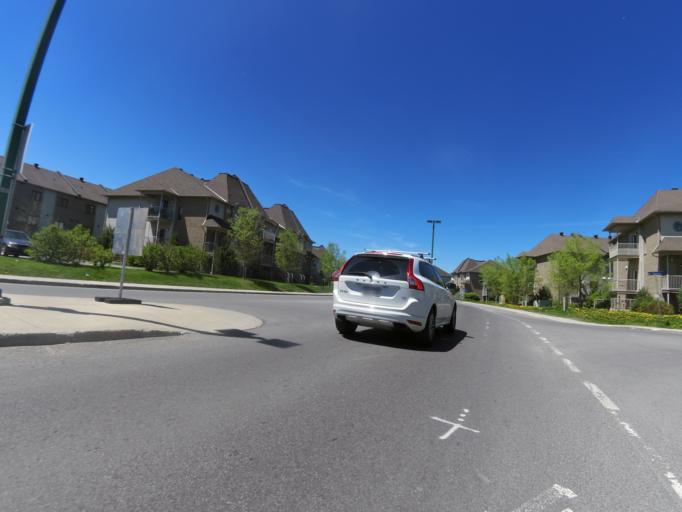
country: CA
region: Ontario
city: Ottawa
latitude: 45.4358
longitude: -75.7809
